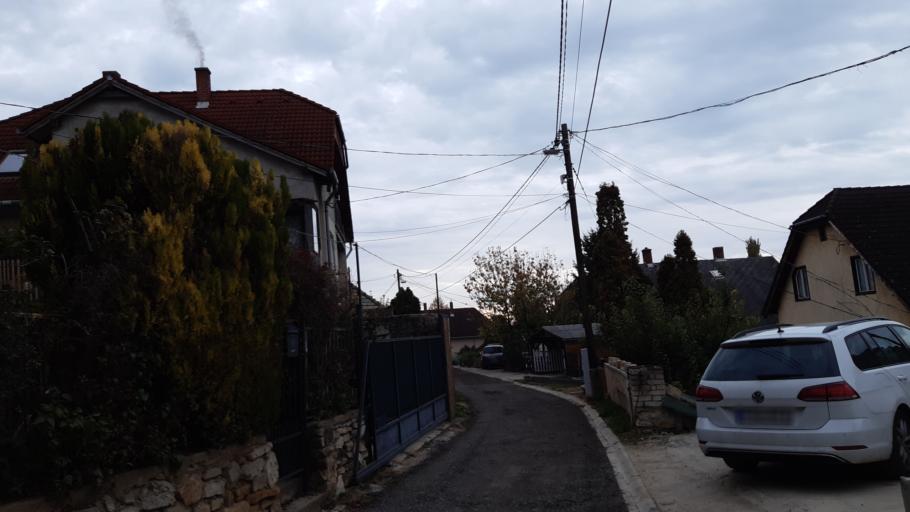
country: HU
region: Veszprem
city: Balatonalmadi
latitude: 47.0456
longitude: 18.0033
